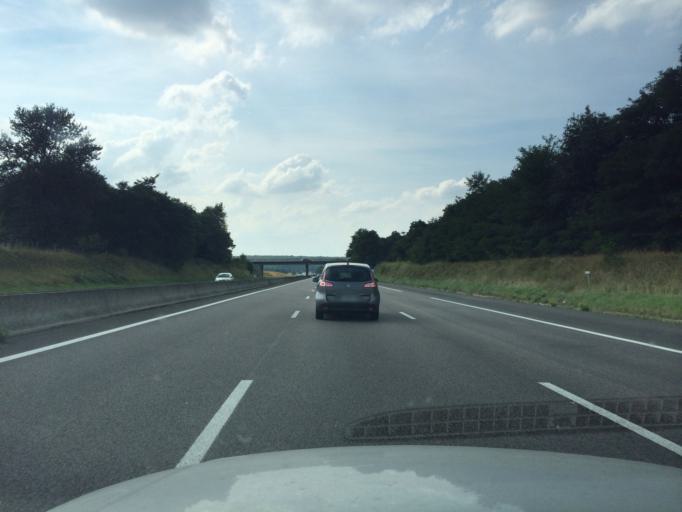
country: FR
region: Ile-de-France
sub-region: Departement des Yvelines
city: Buchelay
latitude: 48.9886
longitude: 1.6566
